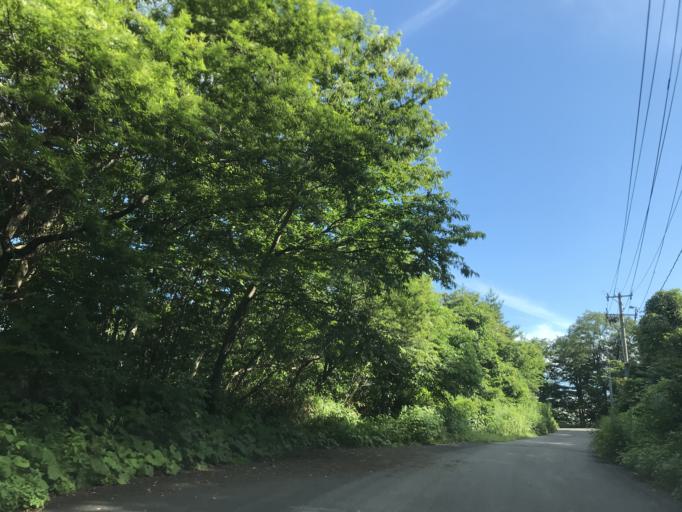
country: JP
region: Iwate
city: Ichinoseki
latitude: 38.8903
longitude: 140.9043
